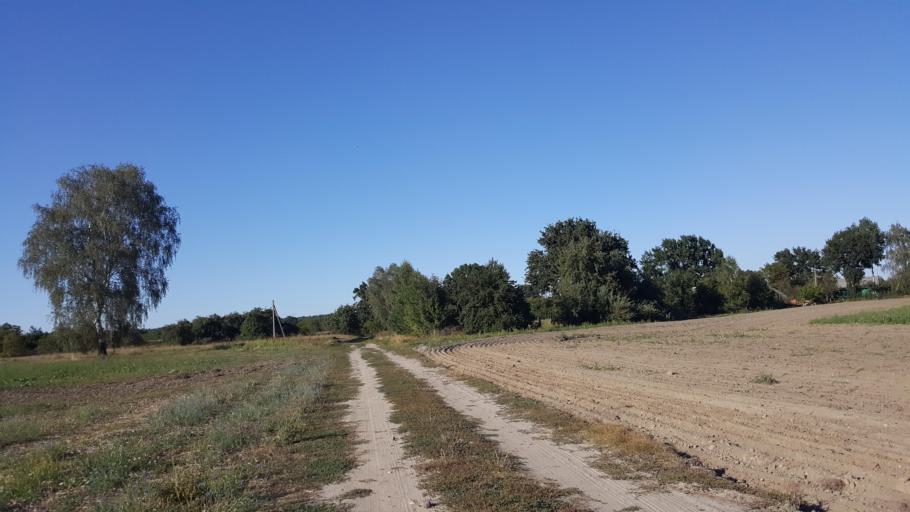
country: BY
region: Brest
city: Vysokaye
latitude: 52.3211
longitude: 23.2624
